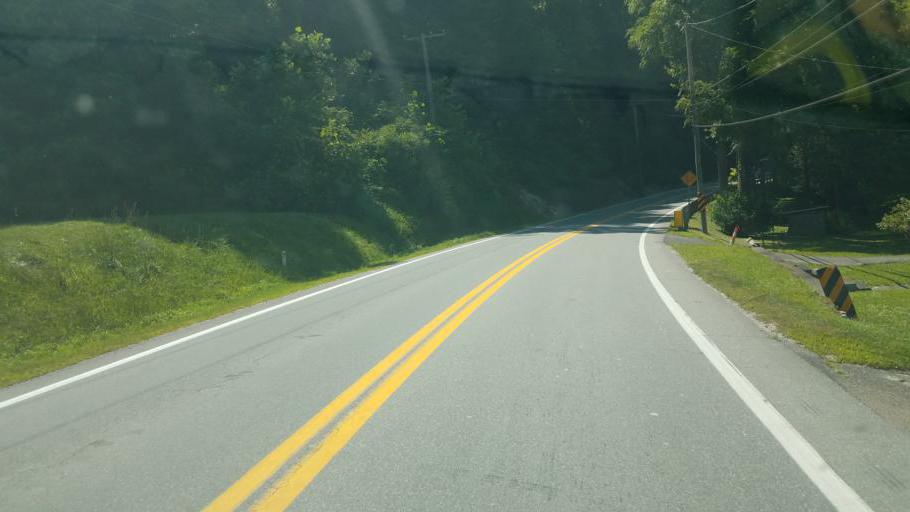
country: US
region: West Virginia
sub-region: Kanawha County
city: Chesapeake
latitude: 38.1820
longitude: -81.4784
